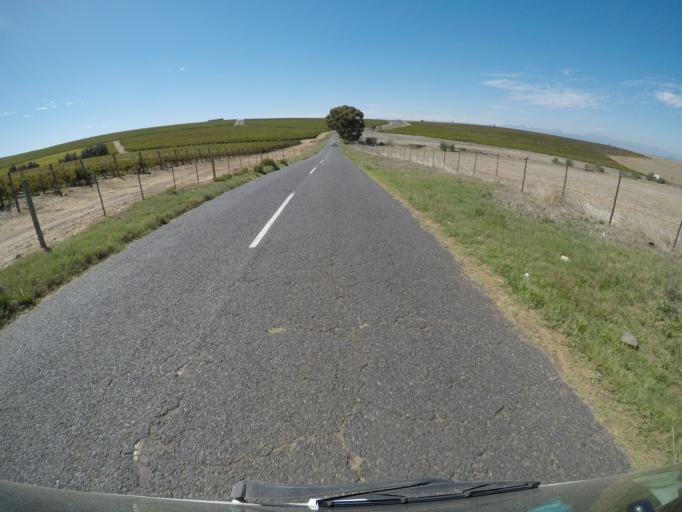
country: ZA
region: Western Cape
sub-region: City of Cape Town
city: Sunset Beach
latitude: -33.7197
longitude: 18.5760
